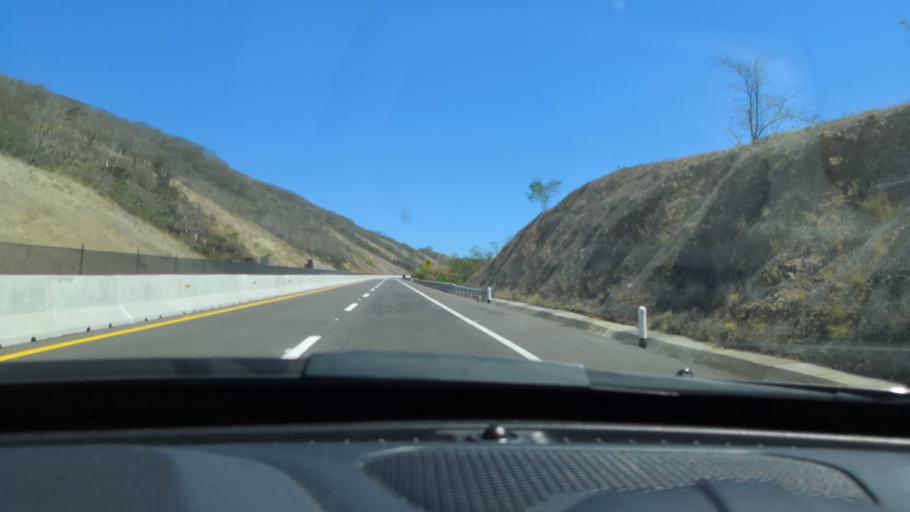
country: MX
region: Nayarit
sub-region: Compostela
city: Juan Escutia (Borbollon)
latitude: 21.1293
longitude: -104.9004
